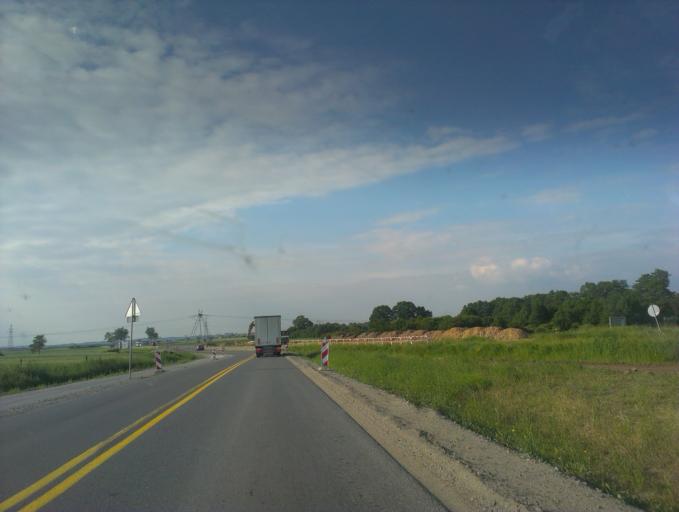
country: PL
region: Lower Silesian Voivodeship
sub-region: Powiat trzebnicki
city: Psary
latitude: 51.2185
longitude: 17.0400
